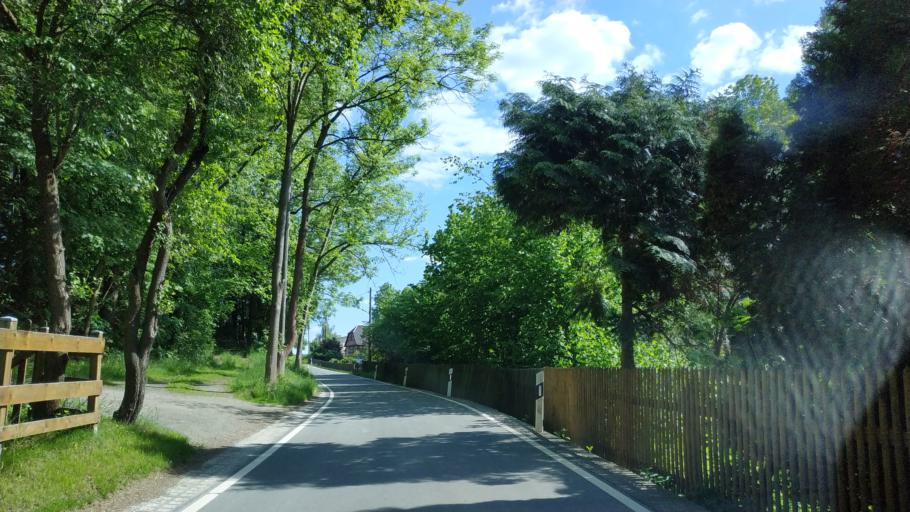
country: DE
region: Saxony
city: Pohl
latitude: 50.5677
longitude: 12.1689
